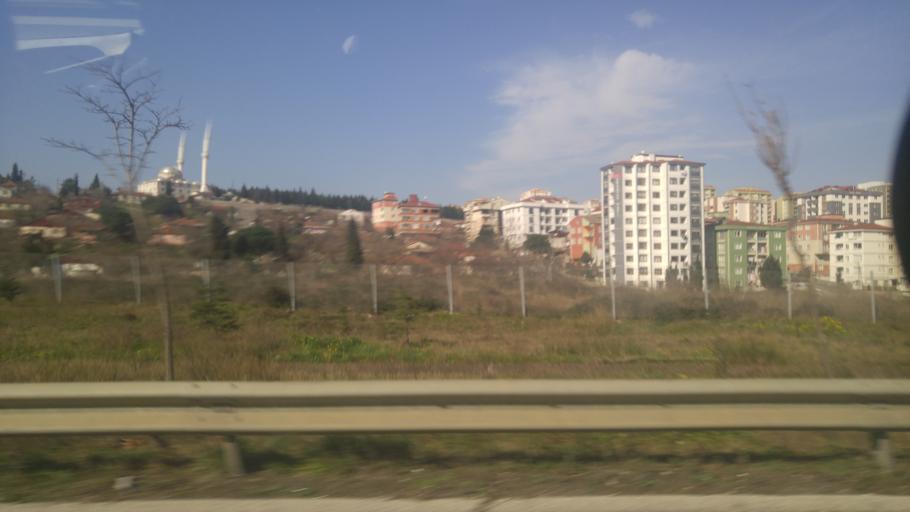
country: TR
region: Kocaeli
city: Darica
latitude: 40.8359
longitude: 29.3713
